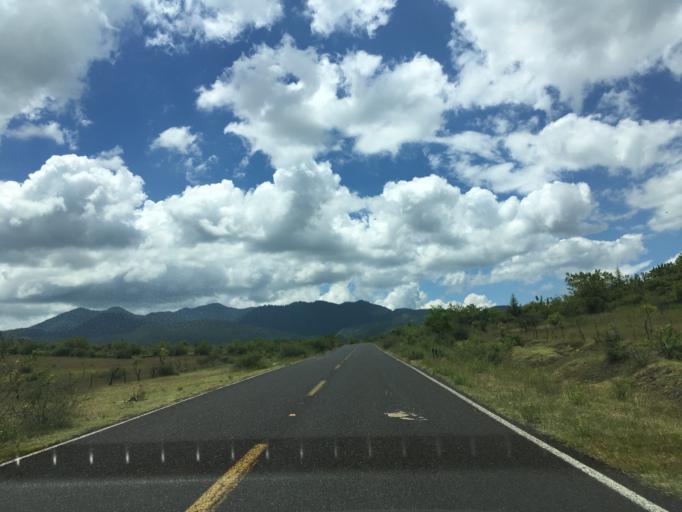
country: MX
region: Mexico
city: Huaniqueo de Morales
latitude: 19.8002
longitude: -101.4555
